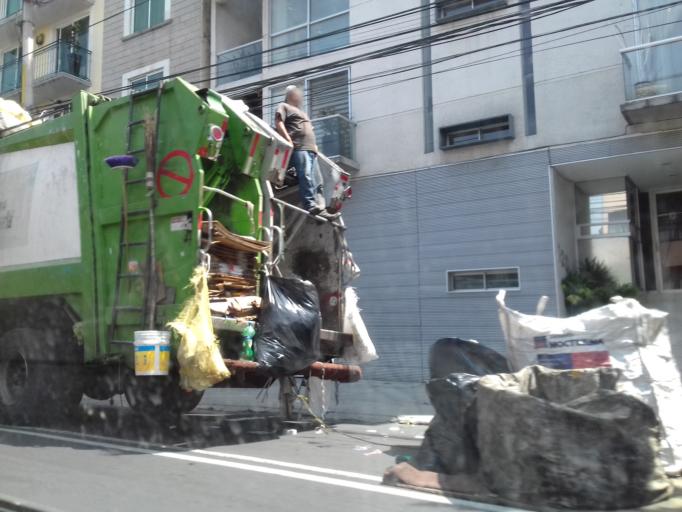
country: MX
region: Mexico City
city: Benito Juarez
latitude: 19.3979
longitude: -99.1614
